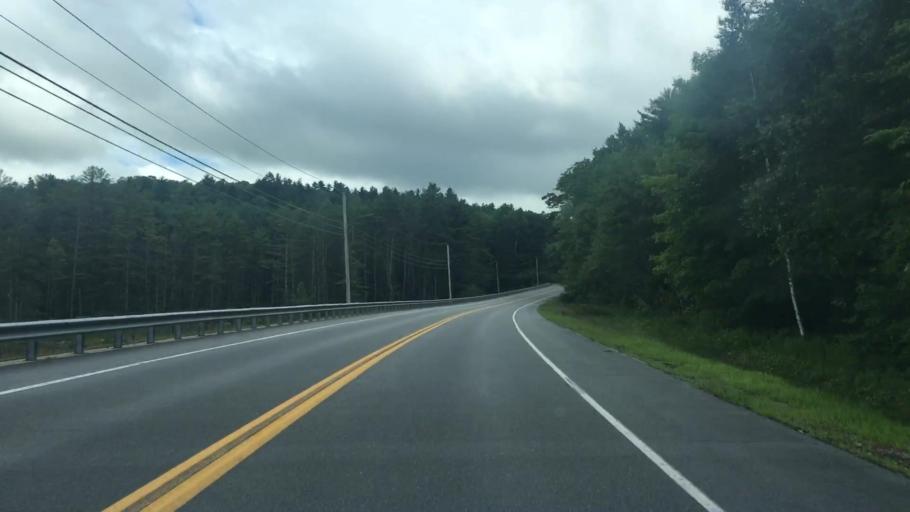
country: US
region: Maine
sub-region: York County
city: Cornish
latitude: 43.7536
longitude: -70.8126
